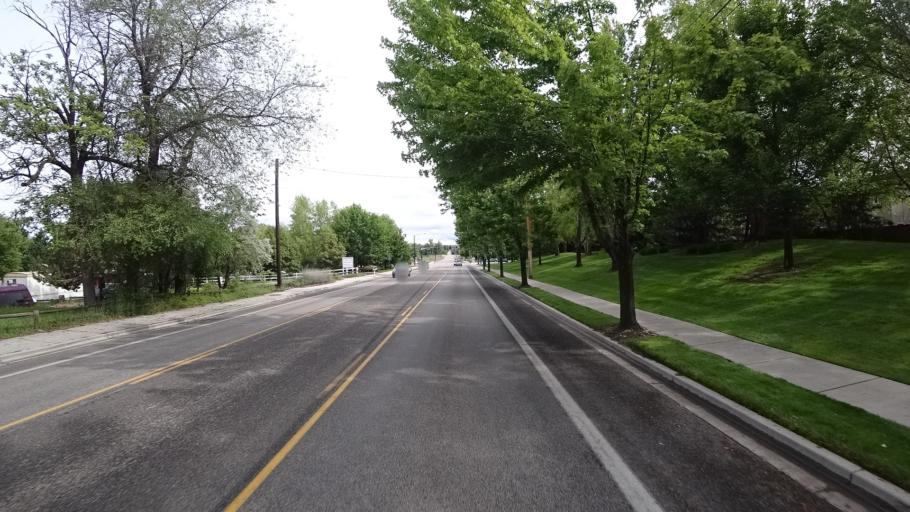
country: US
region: Idaho
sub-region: Ada County
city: Eagle
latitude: 43.7051
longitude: -116.3539
